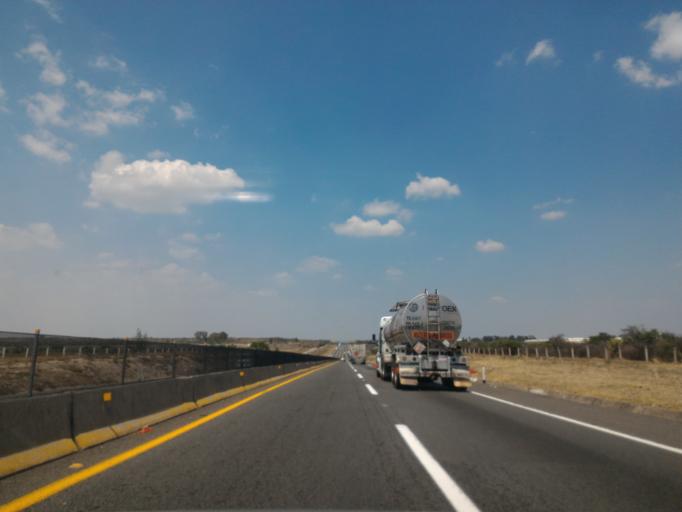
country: MX
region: Jalisco
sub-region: San Juan de los Lagos
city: Colonia Santa Cecilia (La Sauceda)
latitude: 21.1778
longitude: -102.3785
